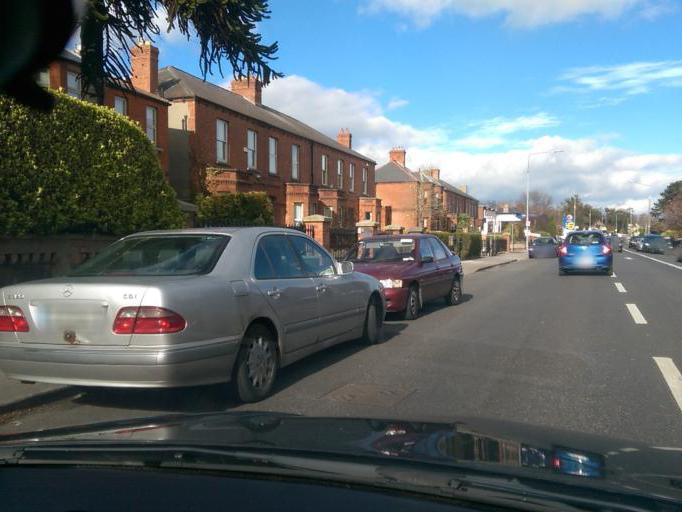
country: IE
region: Leinster
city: Marino
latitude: 53.3651
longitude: -6.2260
